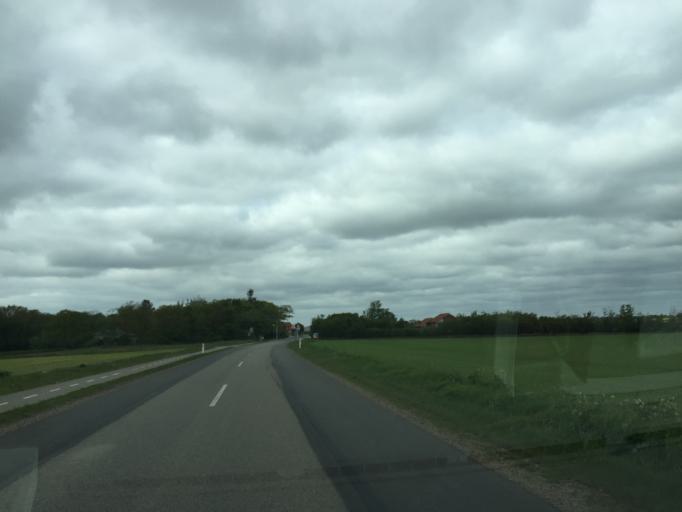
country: DK
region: Central Jutland
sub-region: Ringkobing-Skjern Kommune
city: Ringkobing
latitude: 56.0446
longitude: 8.3144
